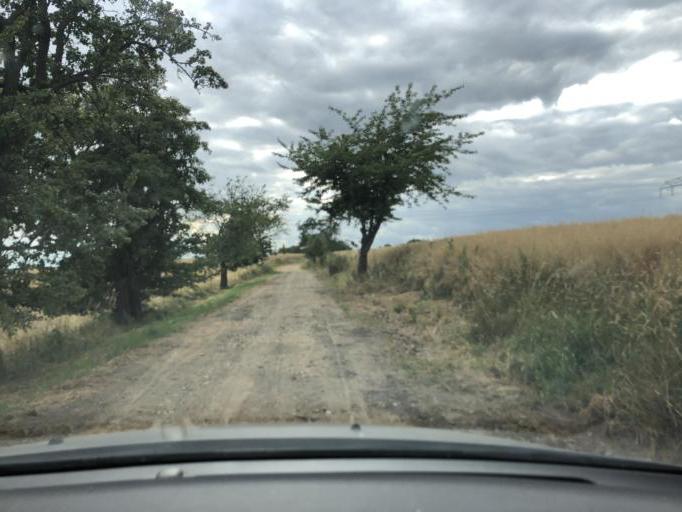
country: DE
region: Saxony
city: Geithain
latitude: 51.0265
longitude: 12.6321
